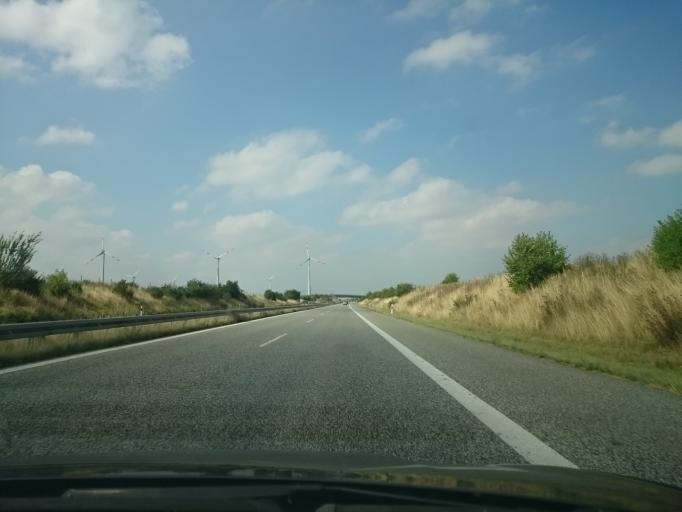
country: DE
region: Brandenburg
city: Schonfeld
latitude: 53.4491
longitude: 13.9819
